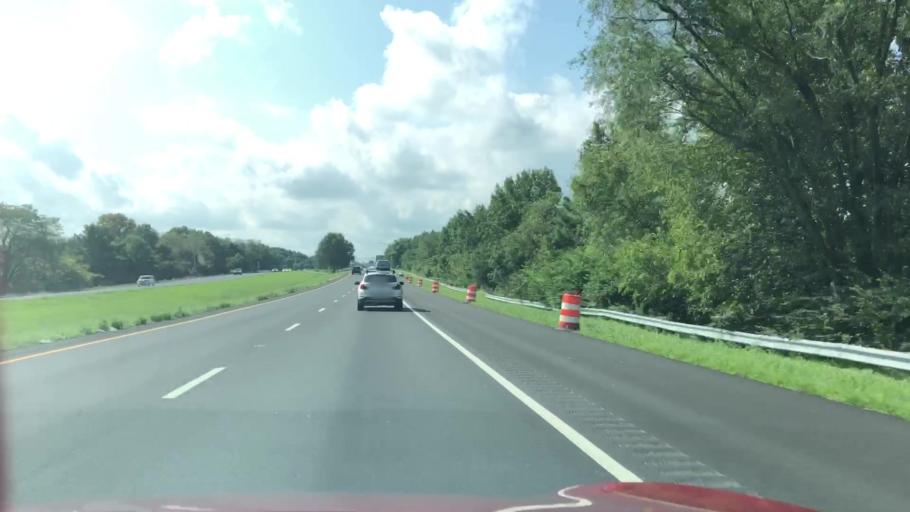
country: US
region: Maryland
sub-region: Wicomico County
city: Salisbury
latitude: 38.3777
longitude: -75.5397
